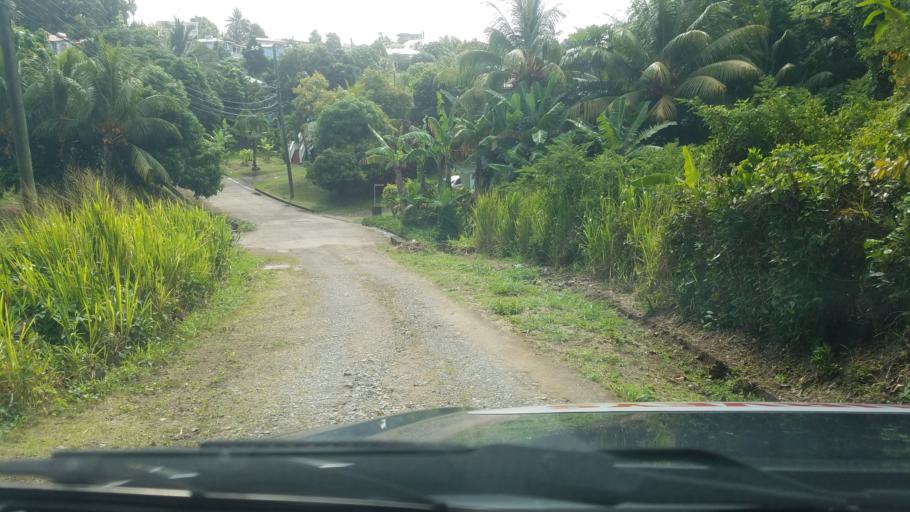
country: LC
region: Castries Quarter
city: Bisee
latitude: 14.0190
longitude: -60.9743
